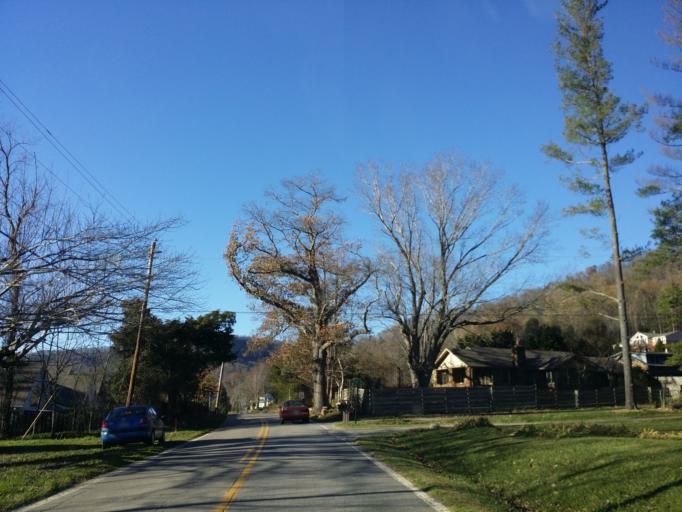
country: US
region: North Carolina
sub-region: Buncombe County
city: Swannanoa
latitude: 35.6167
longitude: -82.4270
